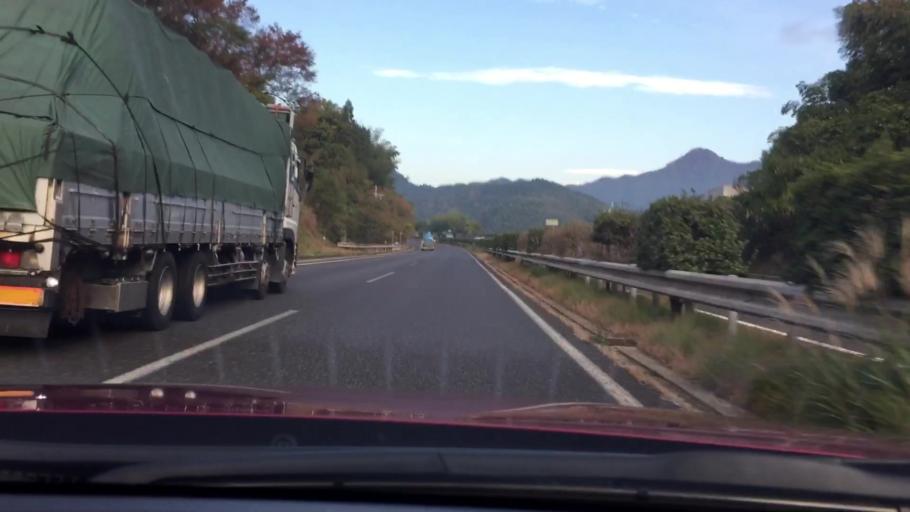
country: JP
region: Hyogo
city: Yamazakicho-nakabirose
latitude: 34.9655
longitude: 134.6779
